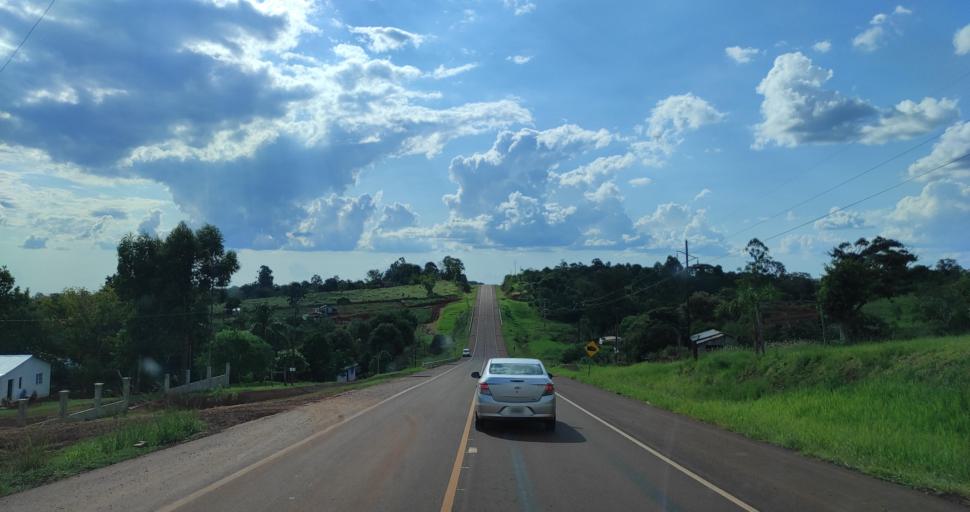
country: AR
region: Misiones
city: Bernardo de Irigoyen
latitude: -26.3765
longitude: -53.9241
